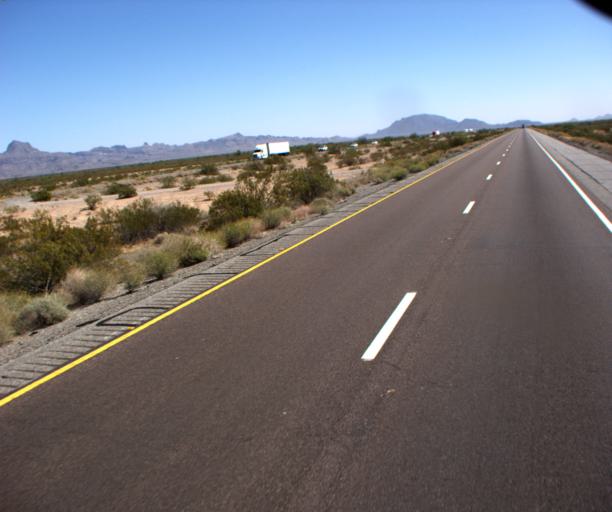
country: US
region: Arizona
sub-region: La Paz County
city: Salome
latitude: 33.5527
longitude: -113.2475
